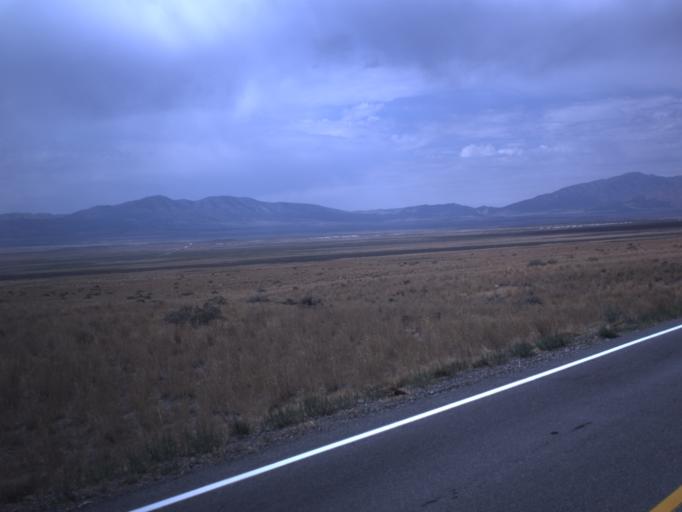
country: US
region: Utah
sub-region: Utah County
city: Eagle Mountain
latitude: 40.2643
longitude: -112.2360
